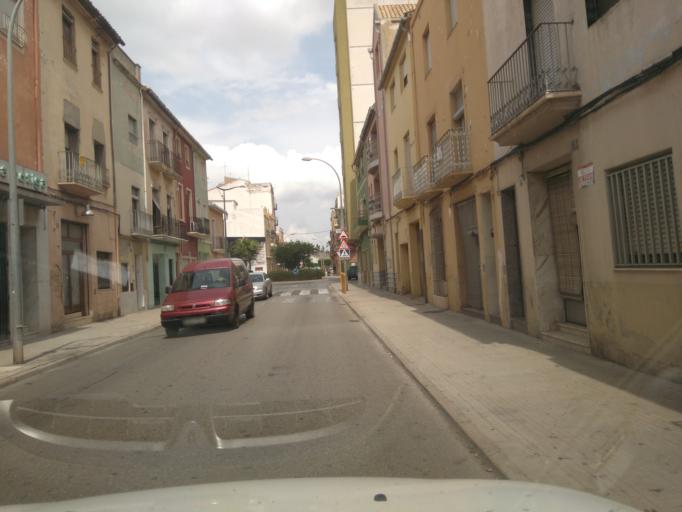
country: ES
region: Valencia
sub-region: Provincia de Valencia
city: Carcaixent
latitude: 39.1258
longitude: -0.4499
